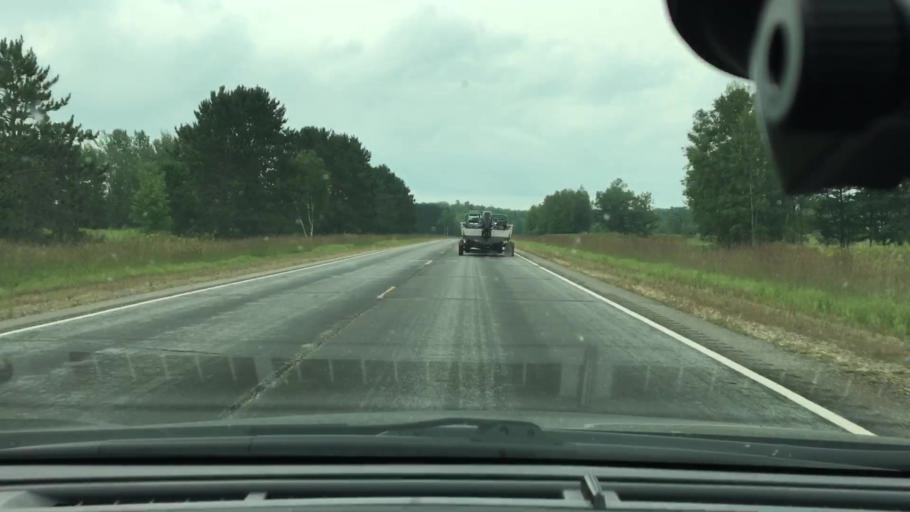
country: US
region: Minnesota
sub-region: Crow Wing County
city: Crosby
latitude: 46.6340
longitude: -93.9481
